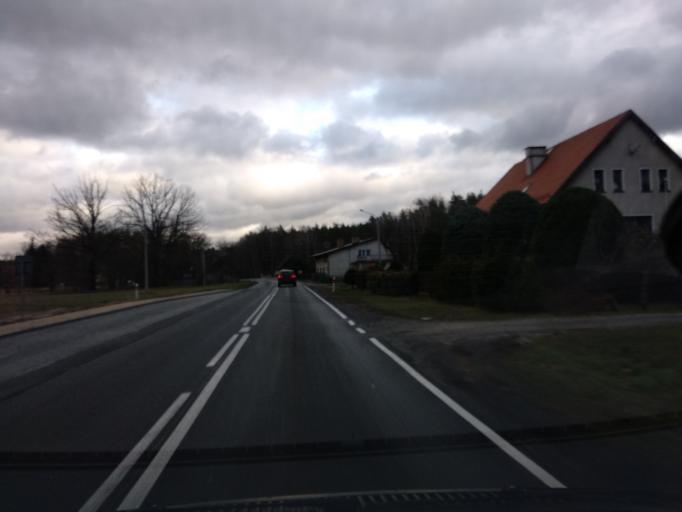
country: PL
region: Lower Silesian Voivodeship
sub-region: Powiat olesnicki
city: Miedzyborz
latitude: 51.4655
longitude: 17.7339
